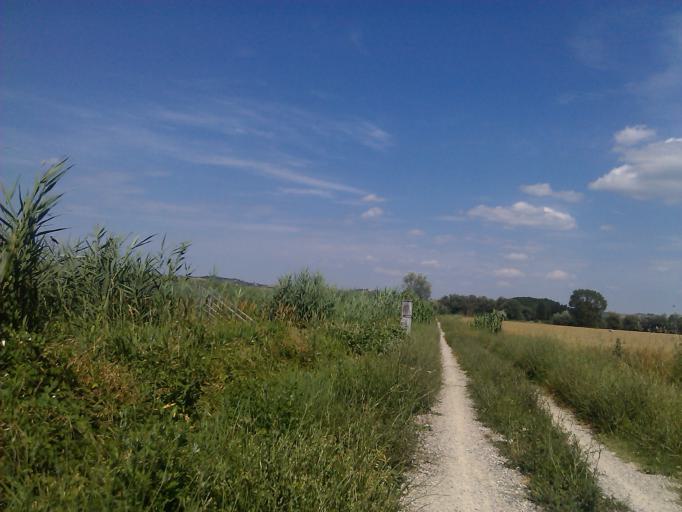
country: IT
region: Tuscany
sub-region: Provincia di Siena
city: Chiusi
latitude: 43.0527
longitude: 11.9435
